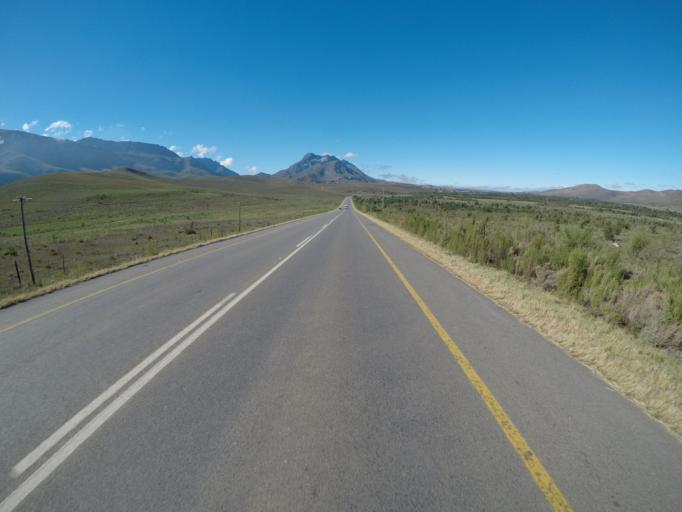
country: ZA
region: Western Cape
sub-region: Overberg District Municipality
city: Caledon
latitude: -34.0491
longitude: 19.5729
